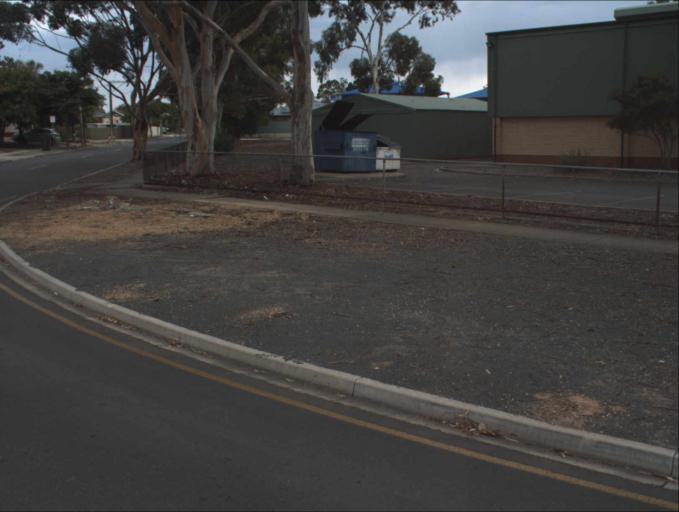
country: AU
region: South Australia
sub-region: Port Adelaide Enfield
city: Enfield
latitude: -34.8483
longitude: 138.6212
